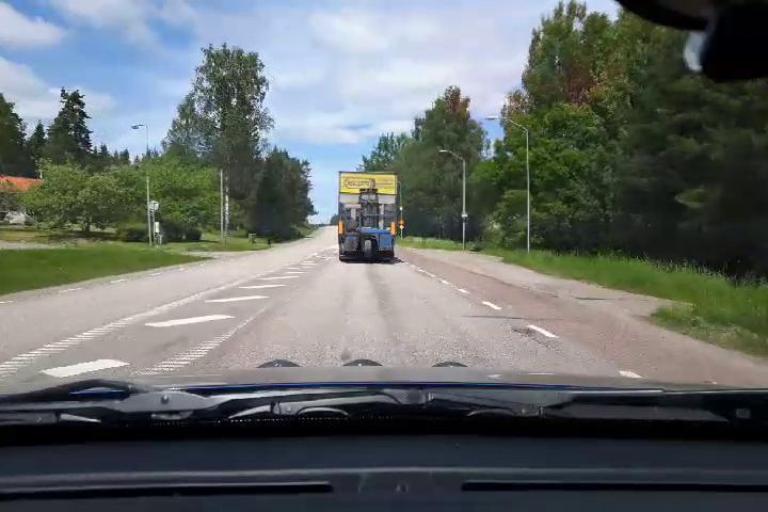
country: SE
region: Uppsala
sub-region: Osthammars Kommun
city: Bjorklinge
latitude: 60.0908
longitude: 17.5547
